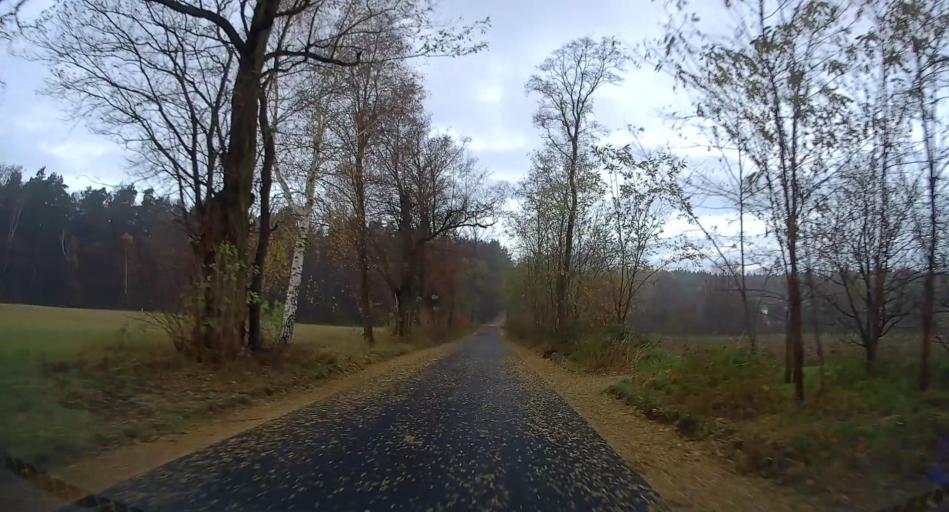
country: PL
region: Lodz Voivodeship
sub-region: Powiat skierniewicki
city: Kowiesy
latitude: 51.9296
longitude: 20.3990
